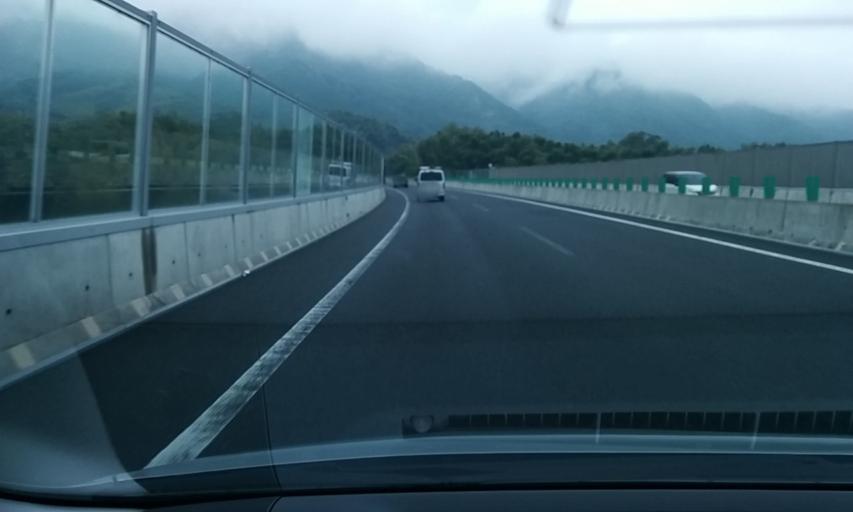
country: JP
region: Kyoto
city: Muko
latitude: 34.9534
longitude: 135.6592
